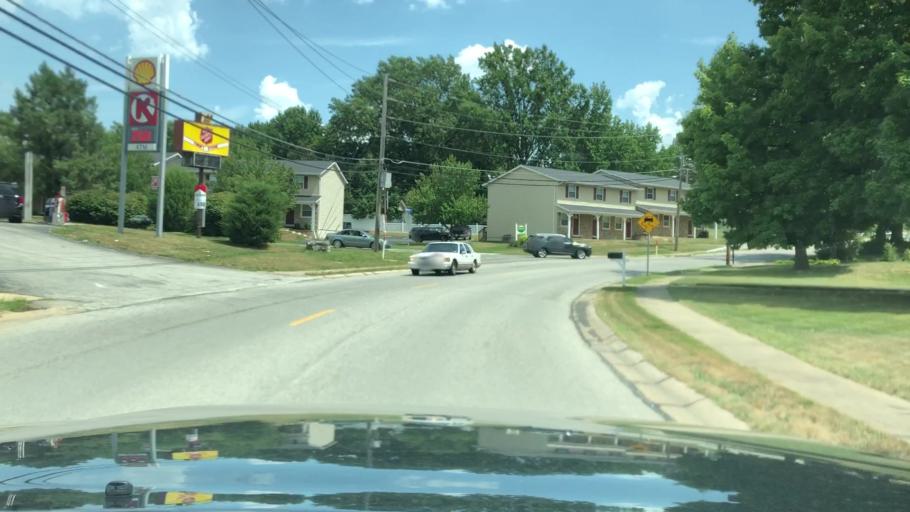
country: US
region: Missouri
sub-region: Saint Charles County
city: Saint Charles
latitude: 38.7927
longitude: -90.5166
